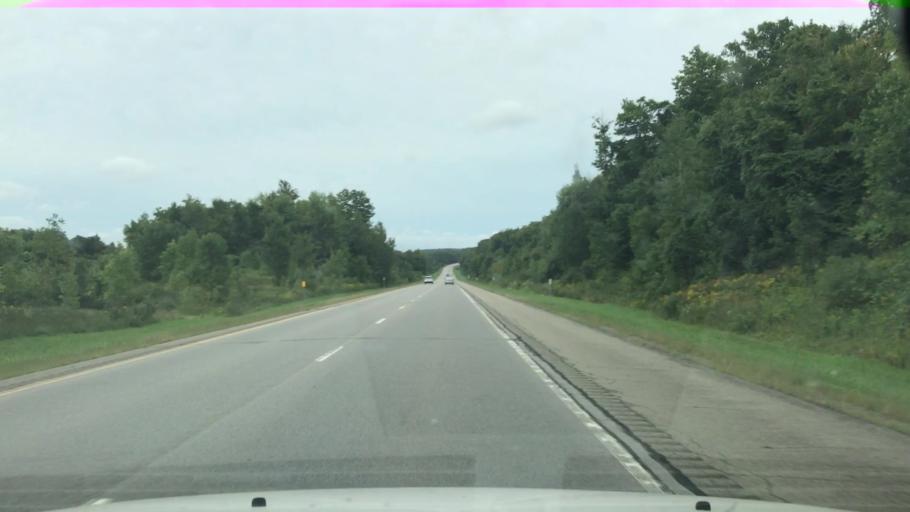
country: US
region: New York
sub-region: Erie County
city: Springville
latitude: 42.5825
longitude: -78.7285
